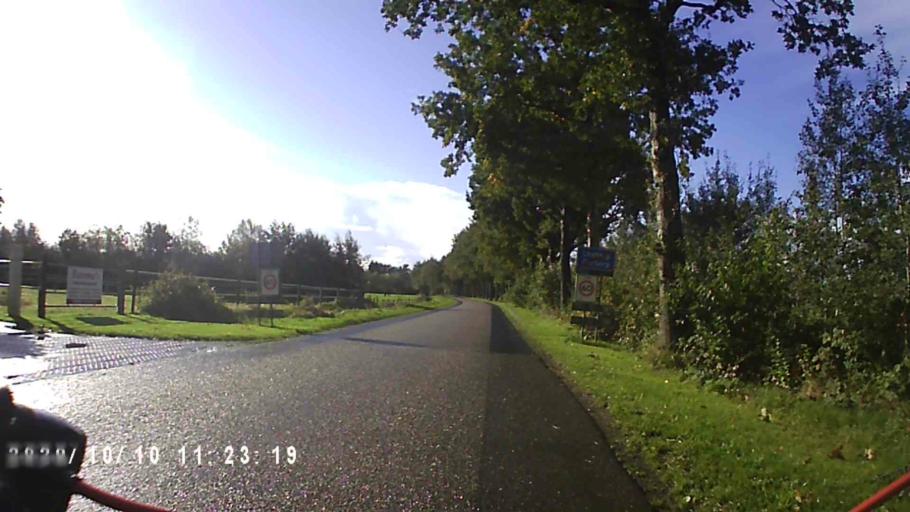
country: NL
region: Friesland
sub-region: Gemeente Smallingerland
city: Drachtstercompagnie
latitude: 53.0904
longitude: 6.1769
